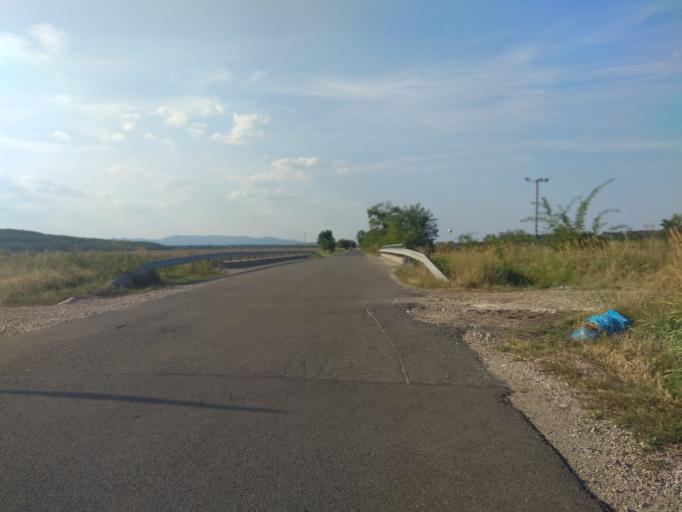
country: HU
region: Borsod-Abauj-Zemplen
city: Harsany
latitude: 47.9057
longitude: 20.7437
